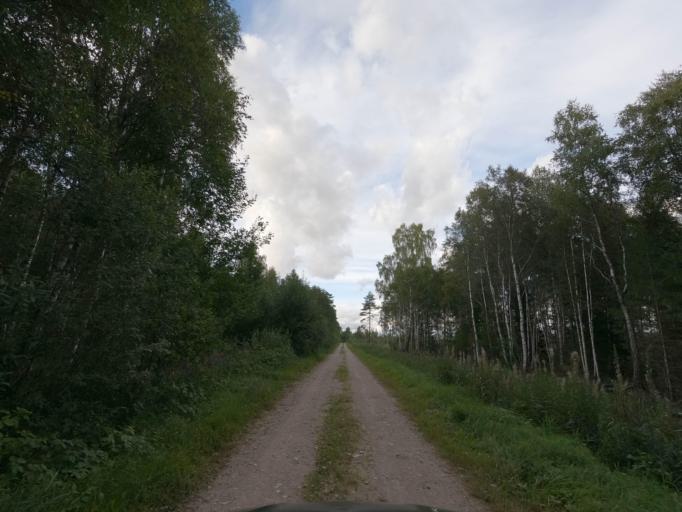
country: EE
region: Raplamaa
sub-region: Rapla vald
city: Rapla
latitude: 59.0082
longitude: 24.7590
